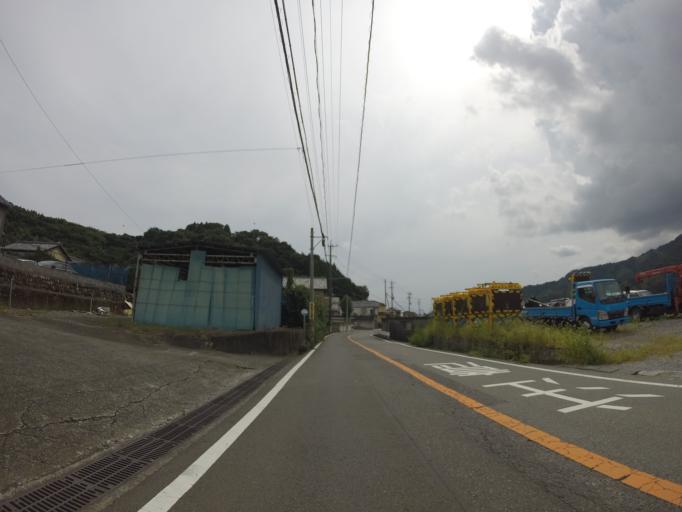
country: JP
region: Shizuoka
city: Fujinomiya
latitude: 35.0708
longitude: 138.5273
